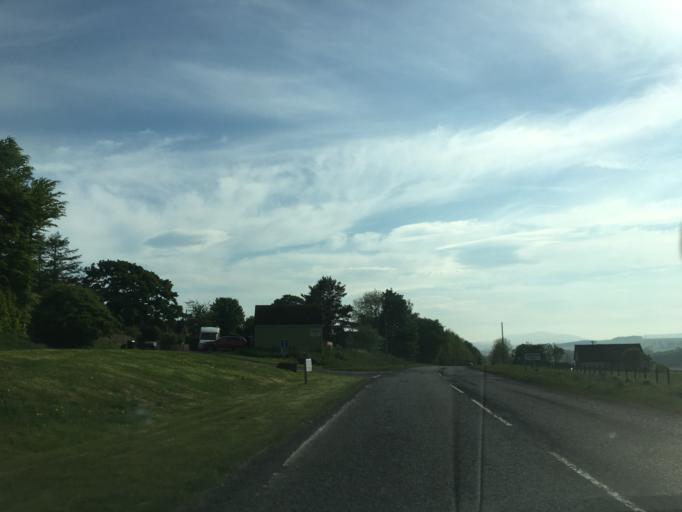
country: GB
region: Scotland
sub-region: The Scottish Borders
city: West Linton
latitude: 55.7545
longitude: -3.2742
